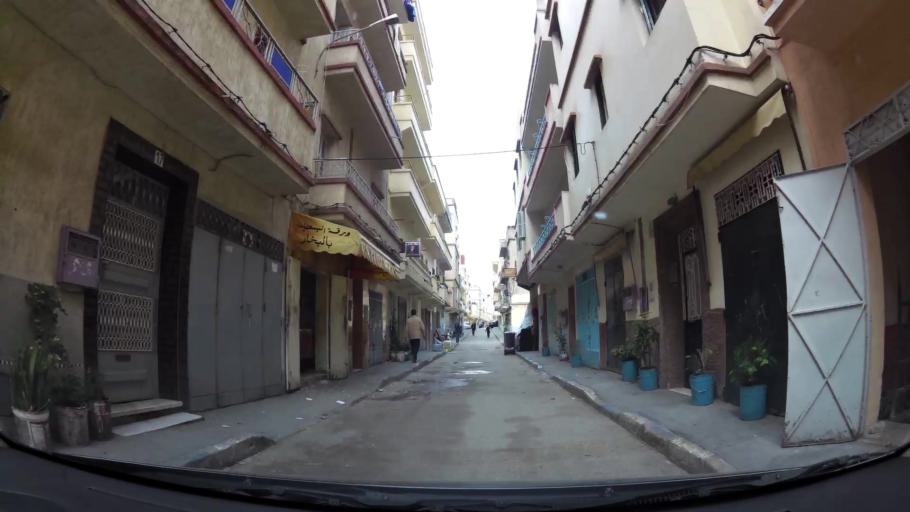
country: MA
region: Tanger-Tetouan
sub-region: Tanger-Assilah
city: Tangier
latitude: 35.7707
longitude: -5.8252
